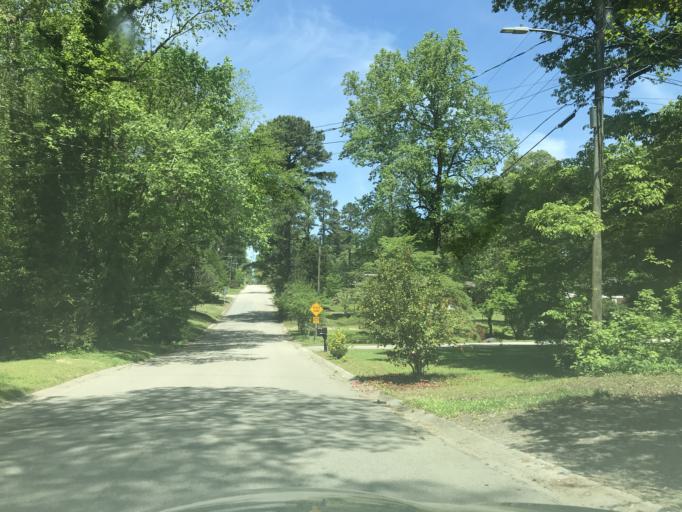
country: US
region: North Carolina
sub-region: Wake County
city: Raleigh
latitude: 35.8262
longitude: -78.5810
